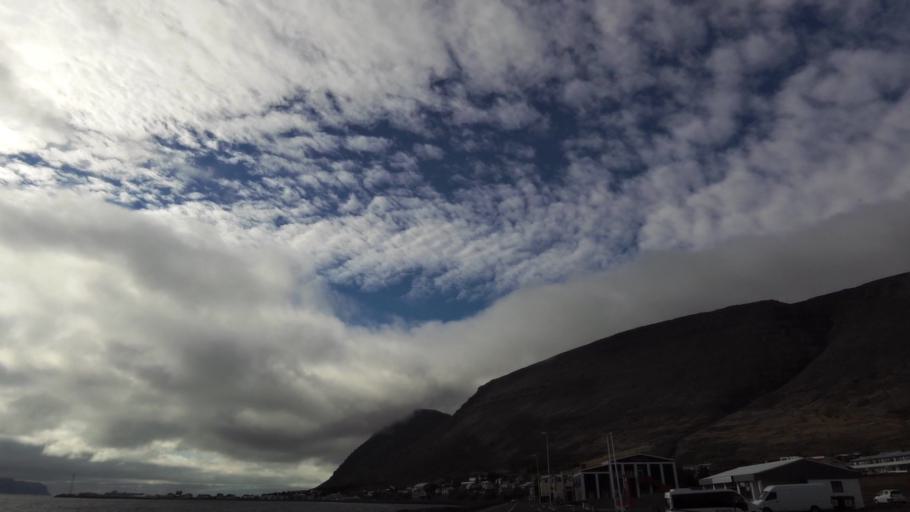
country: IS
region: West
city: Olafsvik
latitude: 65.5904
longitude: -23.9760
